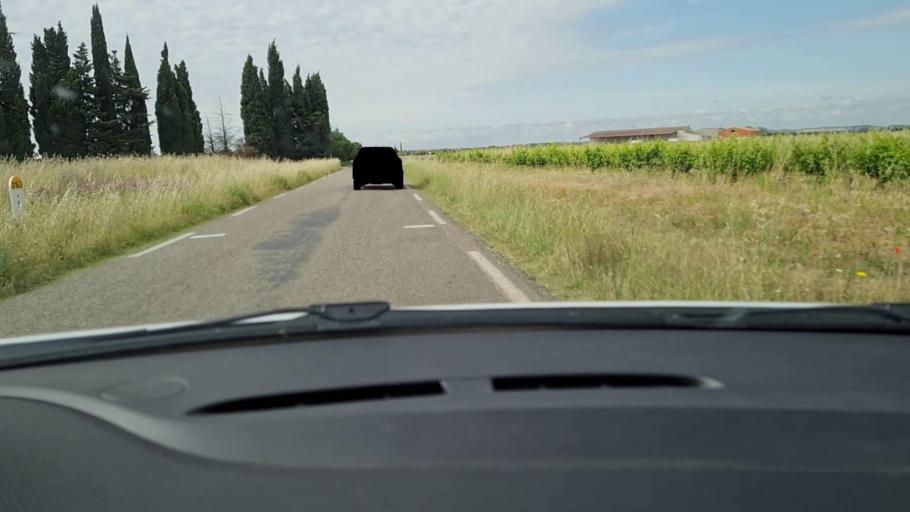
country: FR
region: Languedoc-Roussillon
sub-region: Departement du Gard
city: Bellegarde
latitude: 43.7725
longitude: 4.5181
